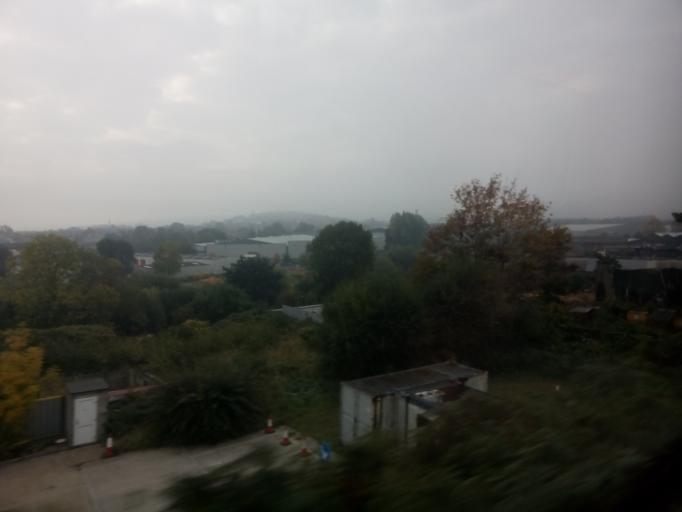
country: GB
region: England
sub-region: Kirklees
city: Dewsbury
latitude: 53.6894
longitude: -1.6367
